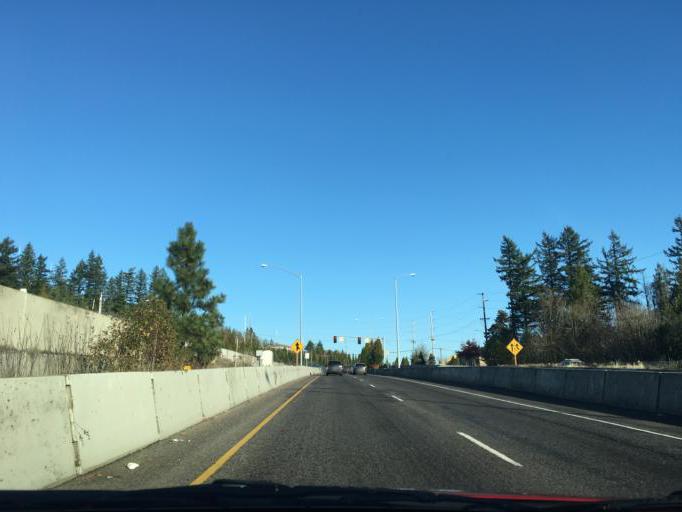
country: US
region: Oregon
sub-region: Washington County
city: West Slope
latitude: 45.5078
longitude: -122.7429
